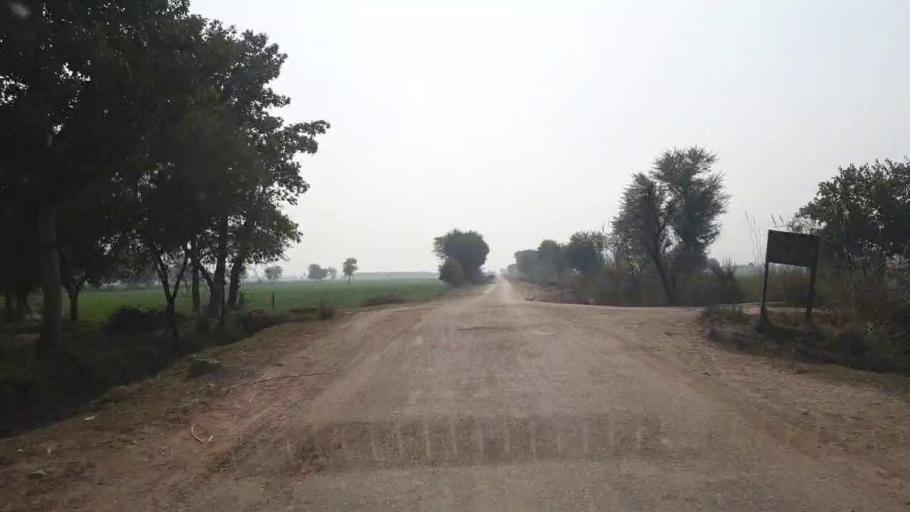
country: PK
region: Sindh
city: Hala
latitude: 25.9239
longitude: 68.4459
